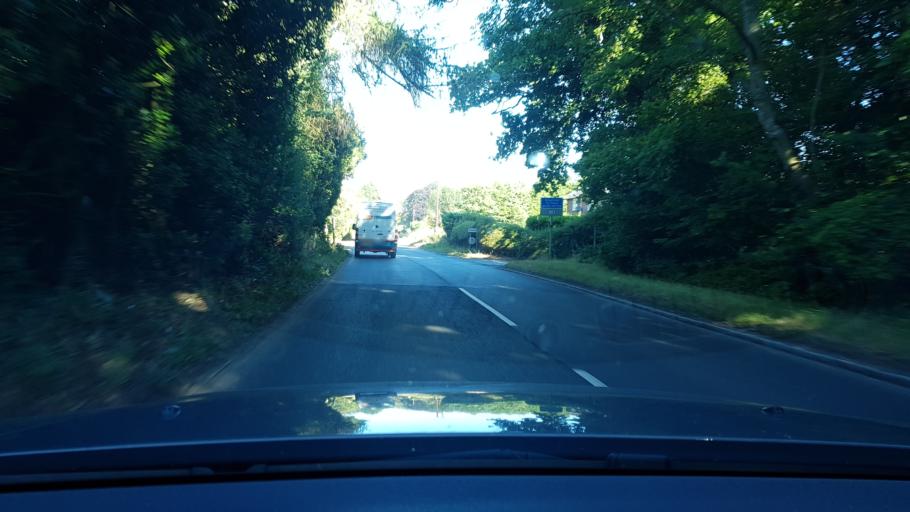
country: GB
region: England
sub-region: West Berkshire
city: Lambourn
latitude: 51.4692
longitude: -1.5090
